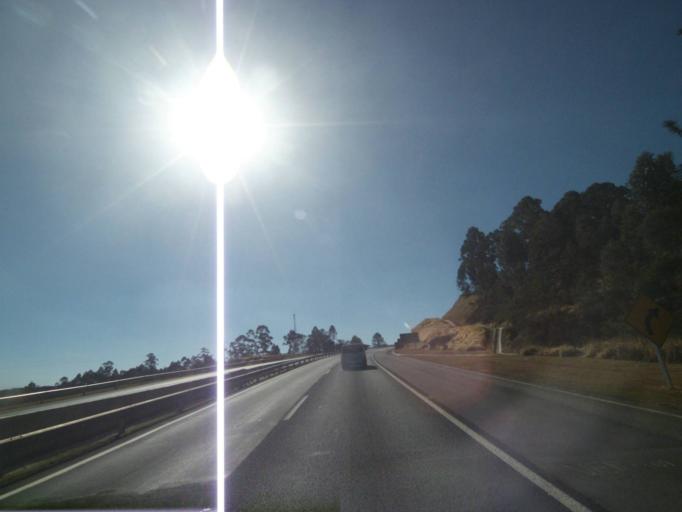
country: BR
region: Parana
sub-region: Tibagi
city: Tibagi
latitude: -24.7518
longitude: -50.5364
